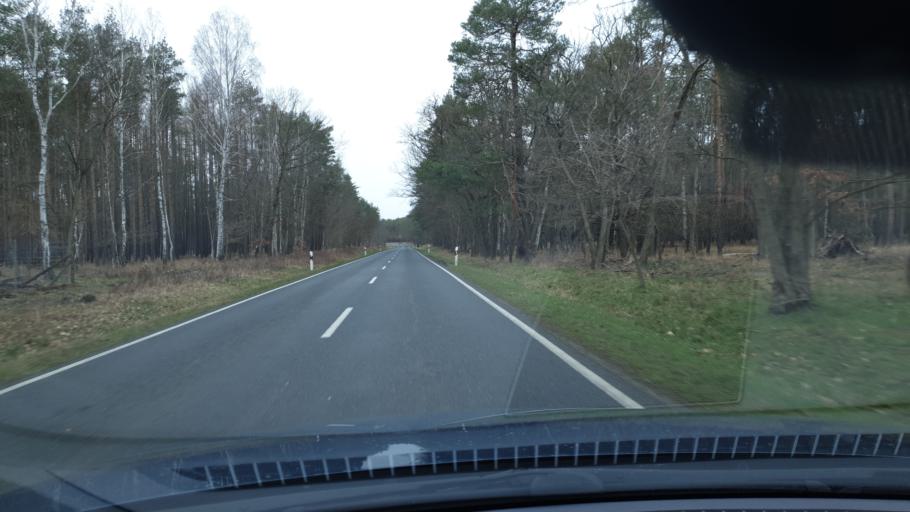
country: DE
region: Saxony-Anhalt
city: Radis
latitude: 51.7677
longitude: 12.4966
